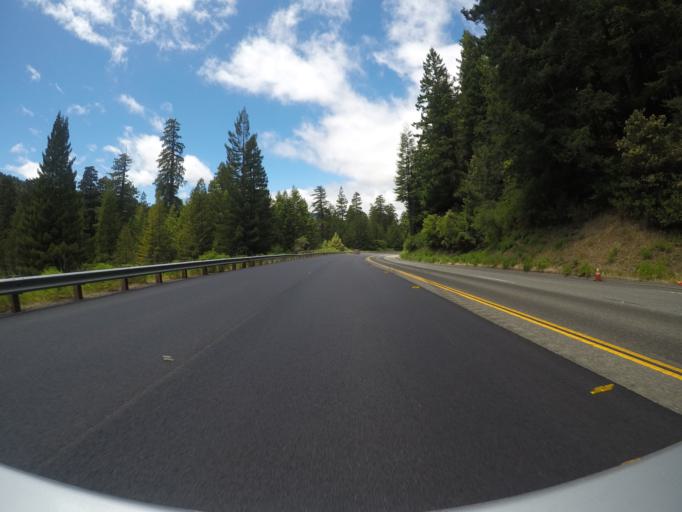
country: US
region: California
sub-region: Humboldt County
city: Redway
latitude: 40.2867
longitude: -123.8945
